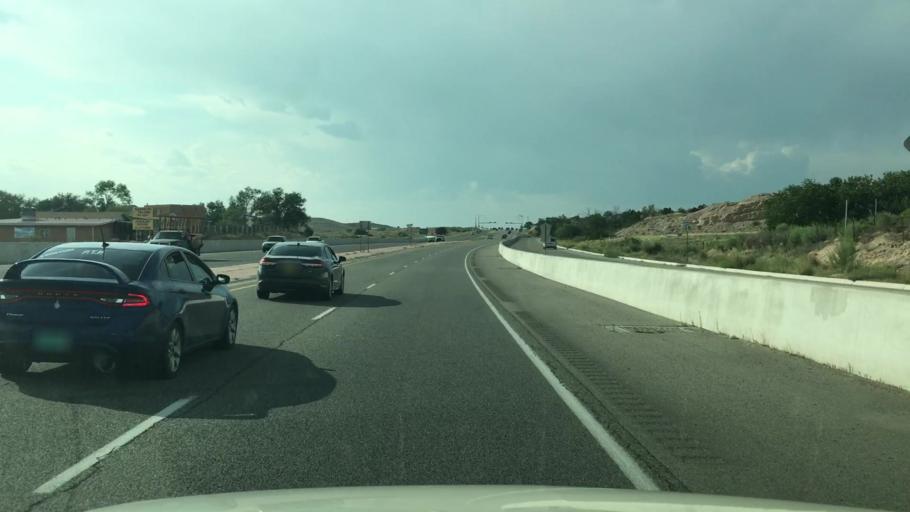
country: US
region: New Mexico
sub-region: Santa Fe County
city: El Valle de Arroyo Seco
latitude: 35.9703
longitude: -106.0390
